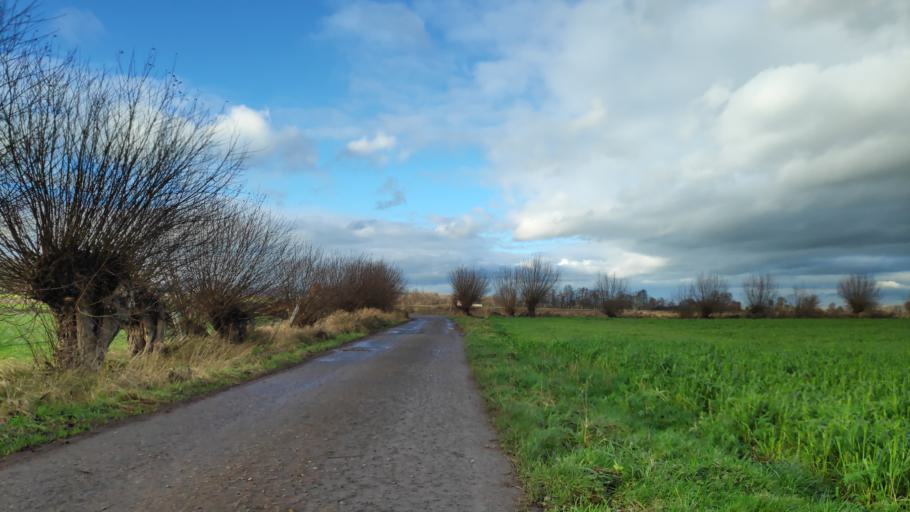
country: DE
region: North Rhine-Westphalia
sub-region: Regierungsbezirk Detmold
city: Minden
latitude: 52.2764
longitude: 8.8537
